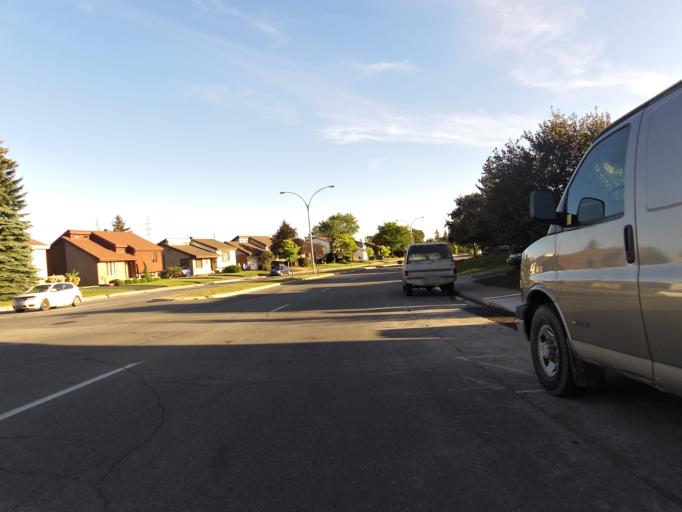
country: CA
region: Ontario
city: Bells Corners
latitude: 45.4144
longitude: -75.8399
